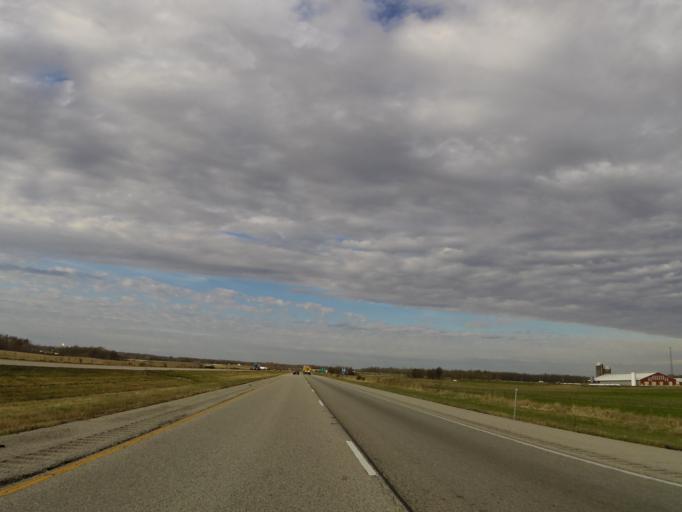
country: US
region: Illinois
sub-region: Washington County
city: Nashville
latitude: 38.3914
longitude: -89.3578
